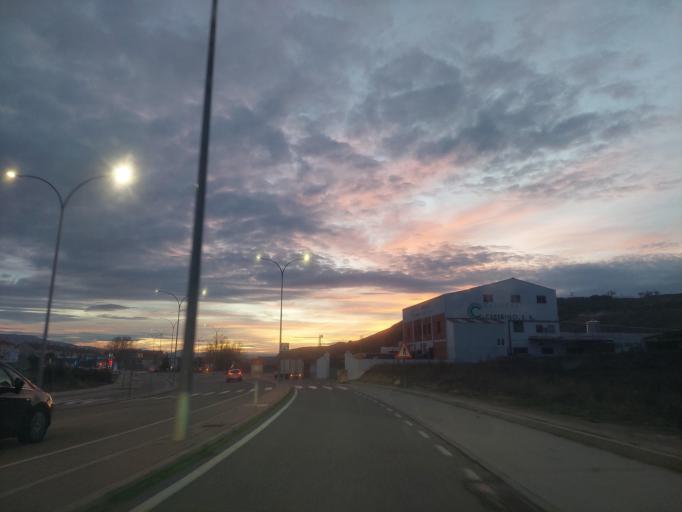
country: ES
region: Castille and Leon
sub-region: Provincia de Segovia
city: La Lastrilla
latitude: 40.9698
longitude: -4.0934
